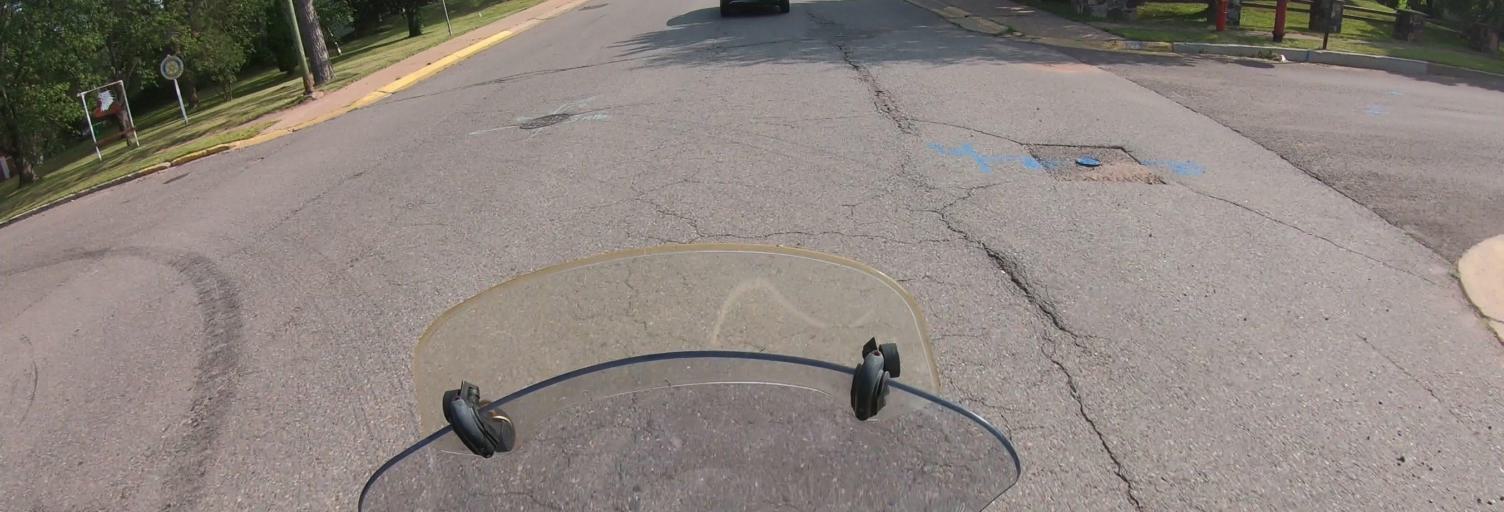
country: US
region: Michigan
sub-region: Gogebic County
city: Wakefield
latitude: 46.4760
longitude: -89.9412
